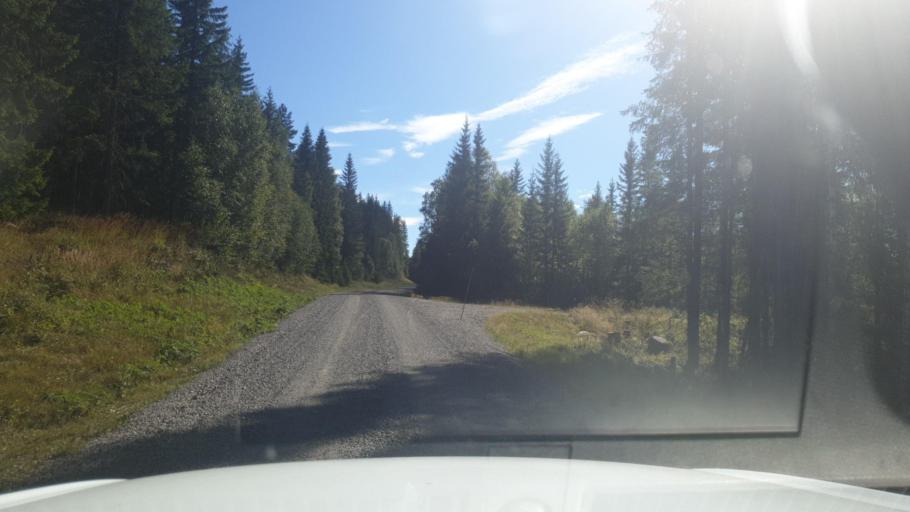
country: SE
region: Vaermland
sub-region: Eda Kommun
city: Charlottenberg
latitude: 60.0970
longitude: 12.6106
